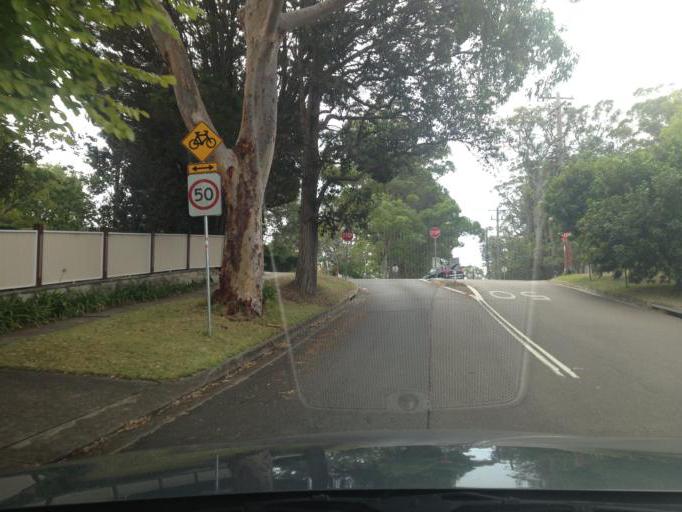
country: AU
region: New South Wales
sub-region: Ku-ring-gai
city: Killara
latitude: -33.7626
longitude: 151.1711
